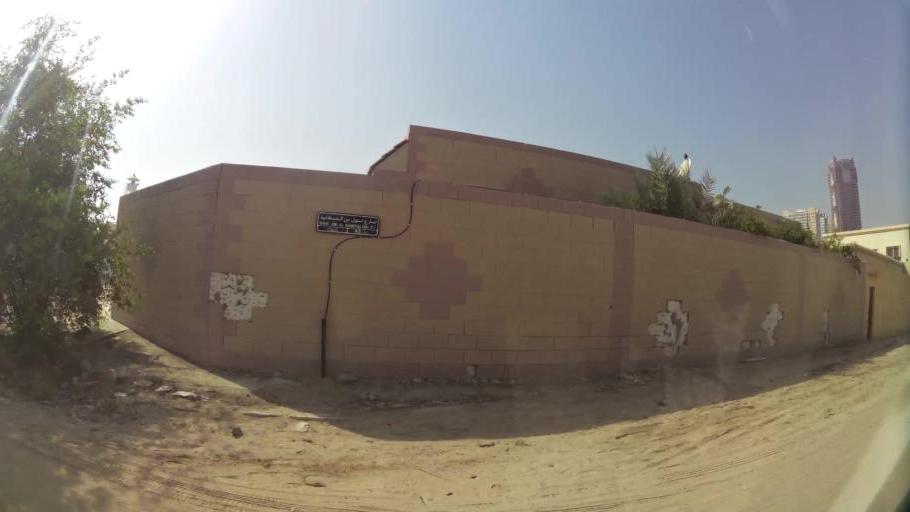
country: AE
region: Ajman
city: Ajman
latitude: 25.3890
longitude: 55.4282
